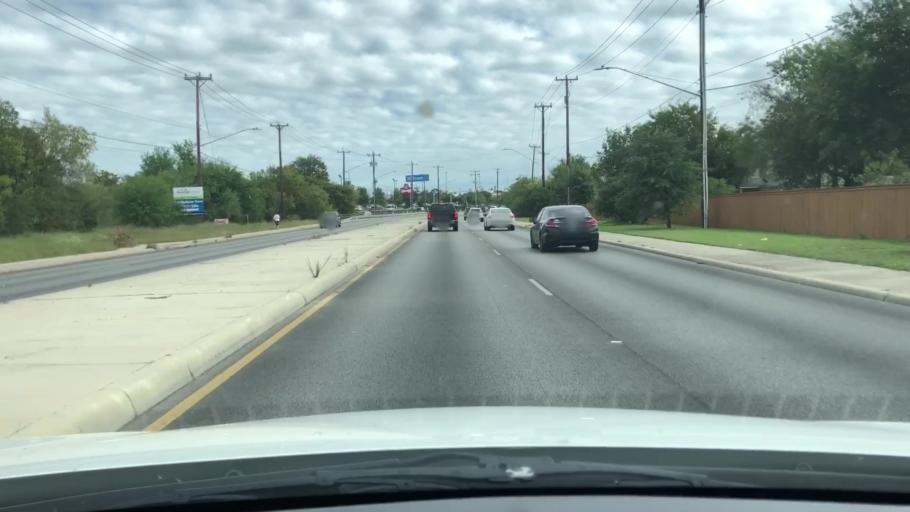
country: US
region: Texas
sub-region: Bexar County
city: Leon Valley
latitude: 29.4876
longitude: -98.6726
